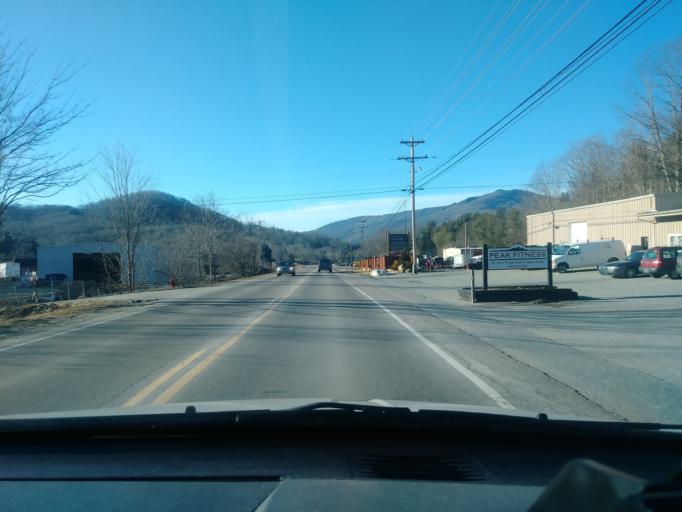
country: US
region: North Carolina
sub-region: Avery County
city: Banner Elk
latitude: 36.1420
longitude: -81.8566
